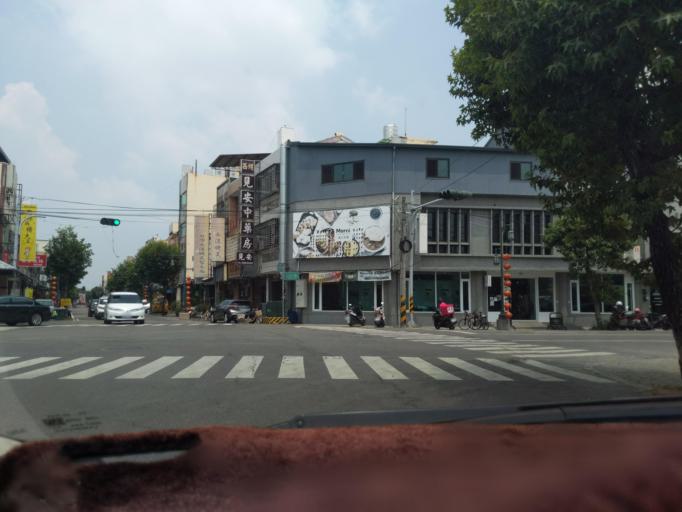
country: TW
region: Taiwan
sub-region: Yunlin
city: Douliu
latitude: 23.8012
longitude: 120.4616
